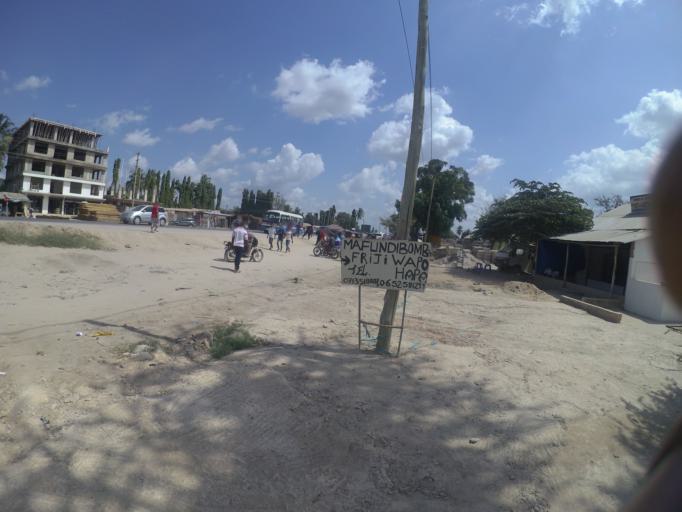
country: TZ
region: Dar es Salaam
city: Magomeni
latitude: -6.6534
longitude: 39.1765
